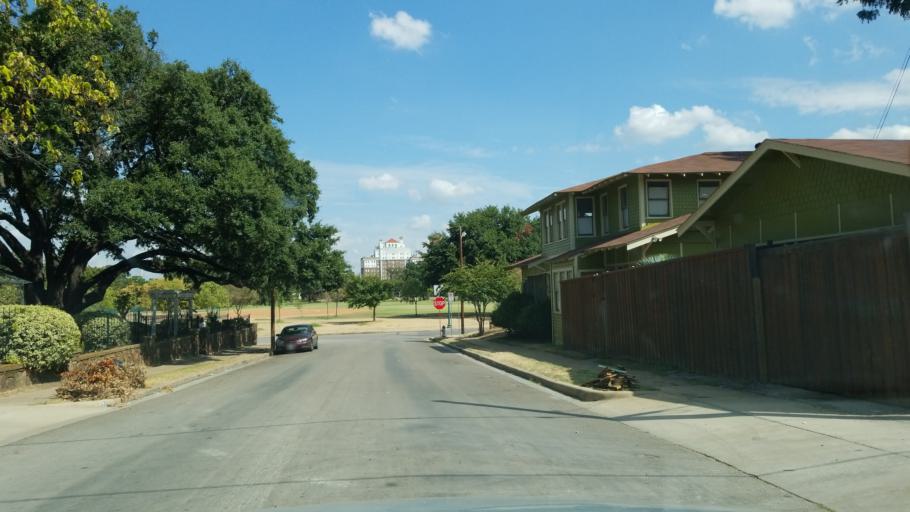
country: US
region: Texas
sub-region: Dallas County
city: Dallas
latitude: 32.7542
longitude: -96.8191
